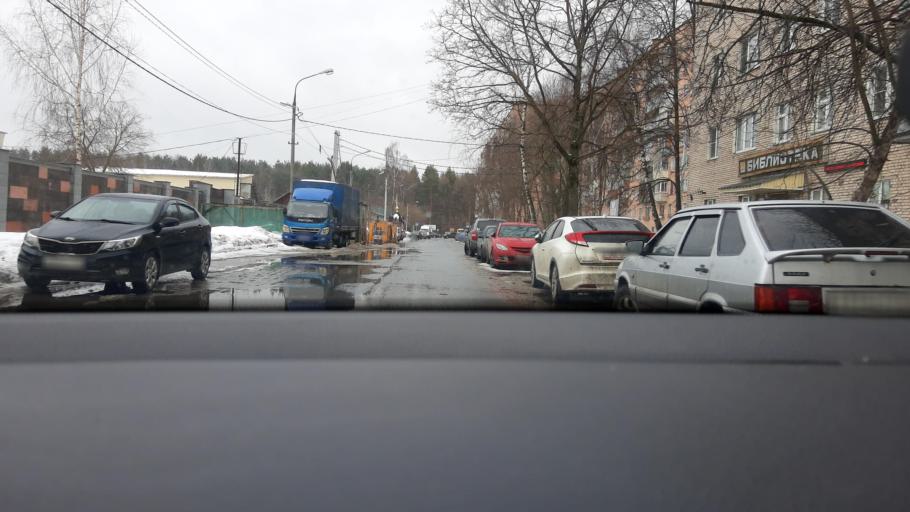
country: RU
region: Moskovskaya
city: Druzhba
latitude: 55.8837
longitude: 37.7550
